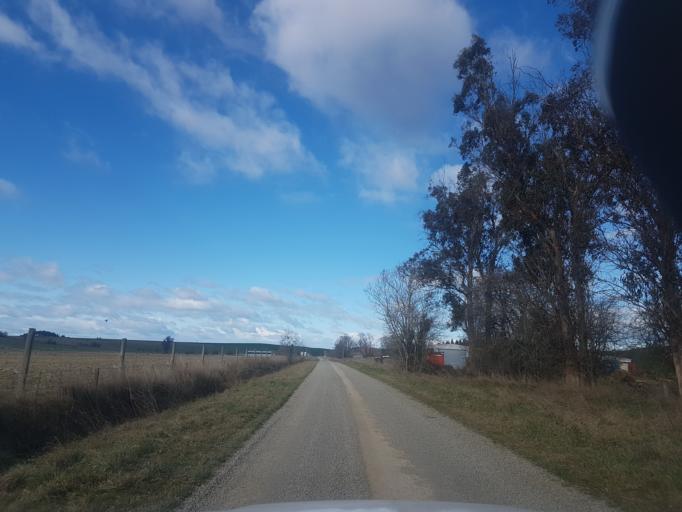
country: NZ
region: Canterbury
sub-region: Timaru District
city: Pleasant Point
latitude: -44.1886
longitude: 171.1944
